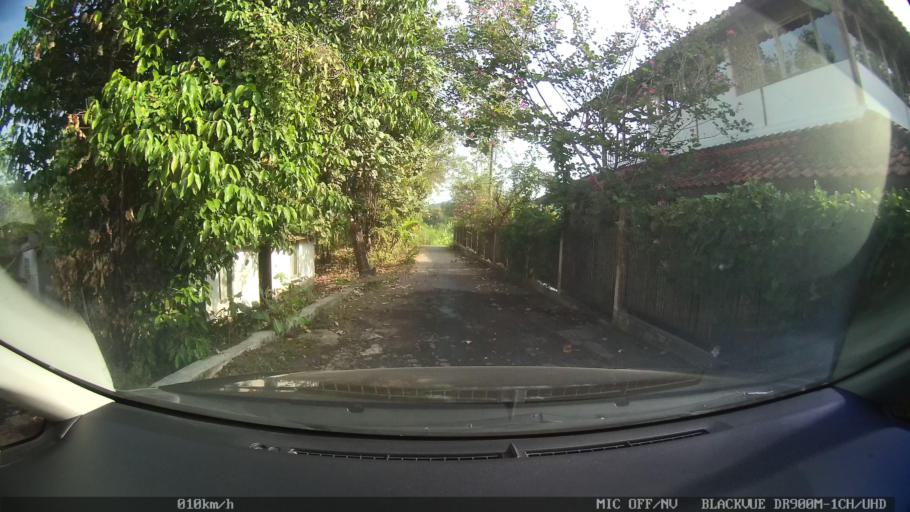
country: ID
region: Daerah Istimewa Yogyakarta
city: Kasihan
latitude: -7.8407
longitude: 110.3171
